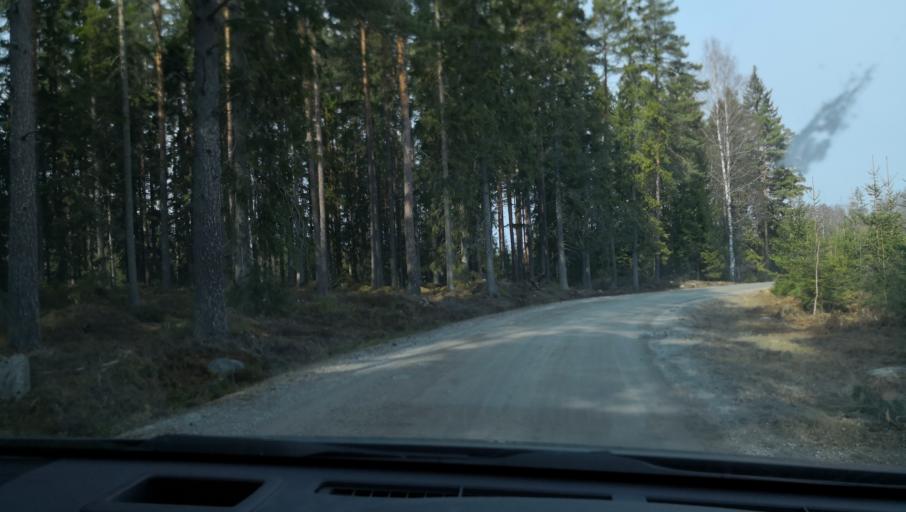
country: SE
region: OErebro
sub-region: Lindesbergs Kommun
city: Frovi
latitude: 59.3612
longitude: 15.4324
